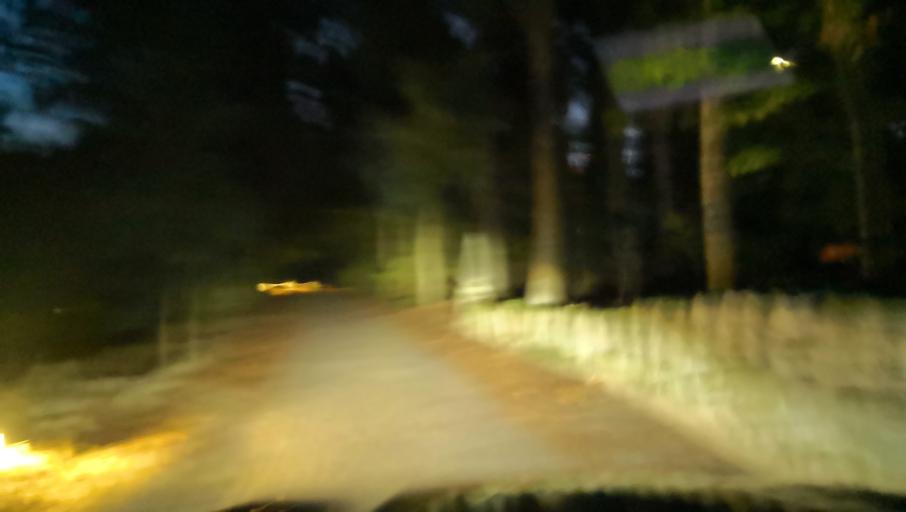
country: PT
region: Vila Real
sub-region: Vila Real
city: Vila Real
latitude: 41.3127
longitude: -7.7300
